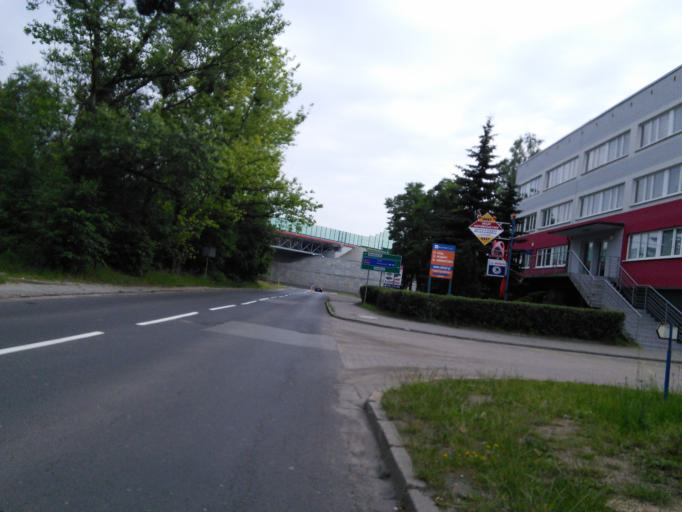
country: PL
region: Silesian Voivodeship
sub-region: Powiat bedzinski
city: Bobrowniki
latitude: 50.3726
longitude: 18.9601
